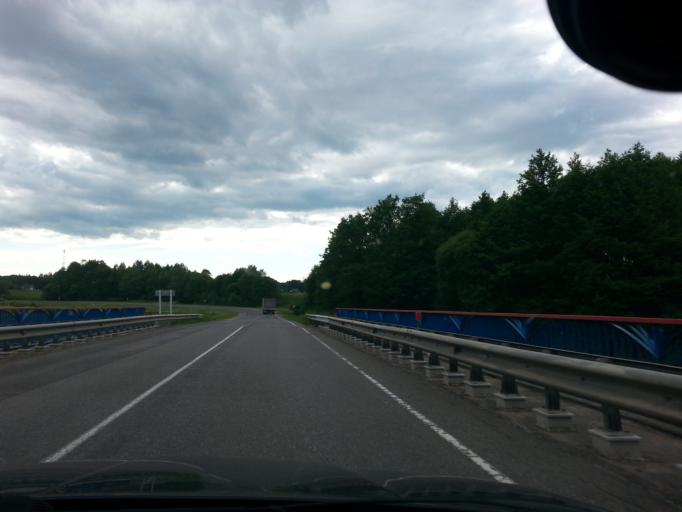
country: BY
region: Minsk
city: Svir
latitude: 54.8617
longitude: 26.3265
